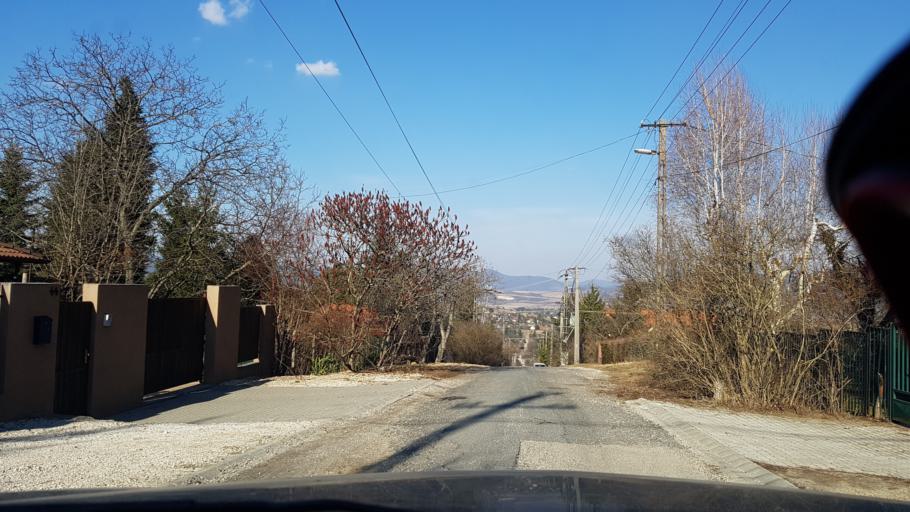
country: HU
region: Pest
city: Solymar
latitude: 47.5904
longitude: 18.9126
